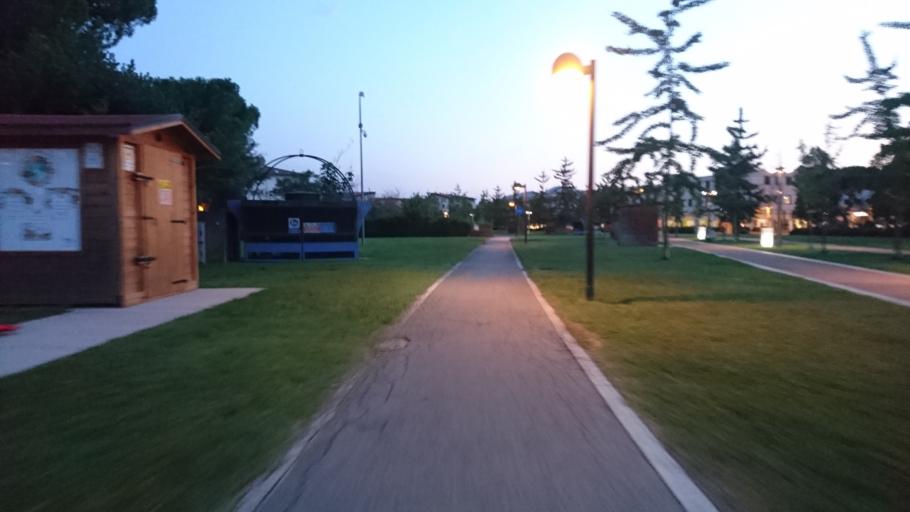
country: IT
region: Veneto
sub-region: Provincia di Padova
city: Abano Terme
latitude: 45.3508
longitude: 11.7832
